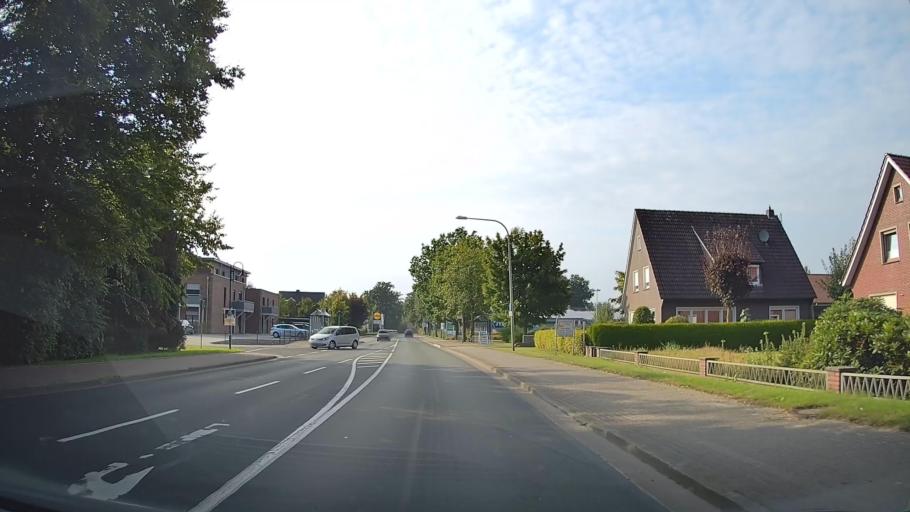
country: DE
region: Lower Saxony
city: Barssel
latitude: 53.1627
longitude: 7.7537
